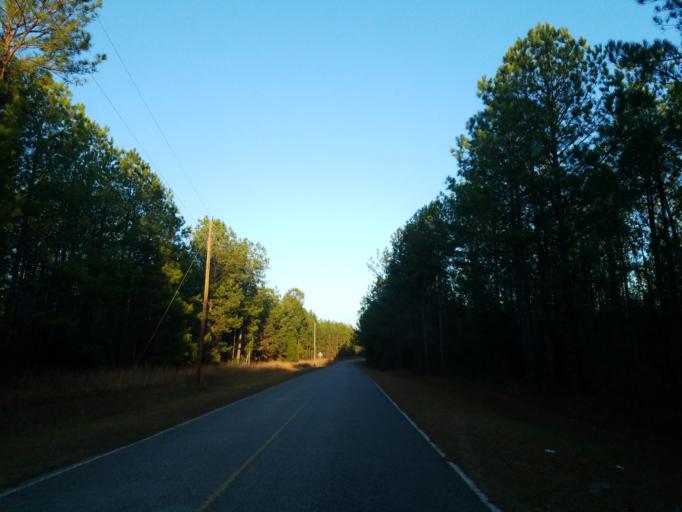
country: US
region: Mississippi
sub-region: Clarke County
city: Stonewall
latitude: 32.2623
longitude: -88.8068
